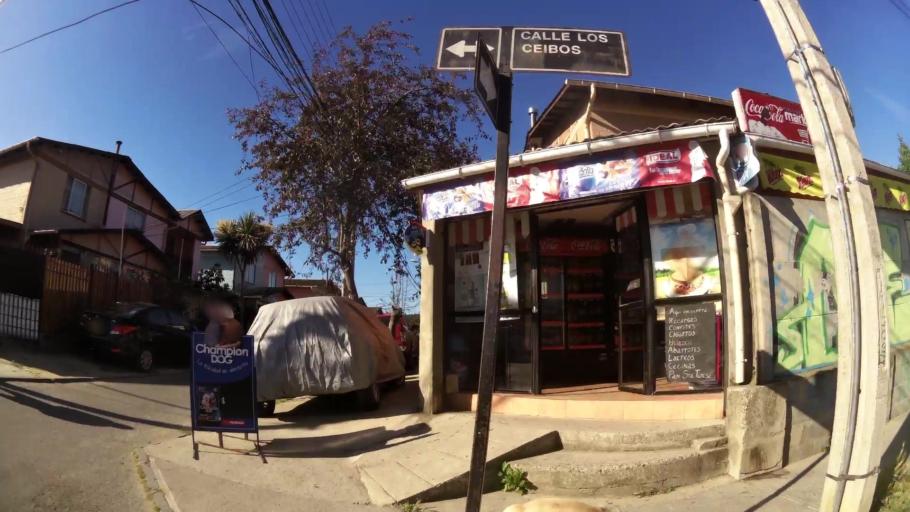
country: CL
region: Valparaiso
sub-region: Provincia de Valparaiso
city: Valparaiso
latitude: -33.1175
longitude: -71.5782
